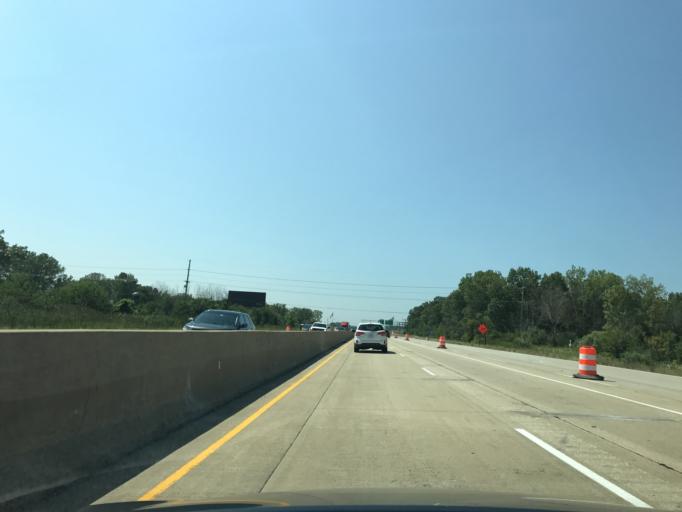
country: US
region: Indiana
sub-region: LaPorte County
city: Trail Creek
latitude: 41.6583
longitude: -86.8824
